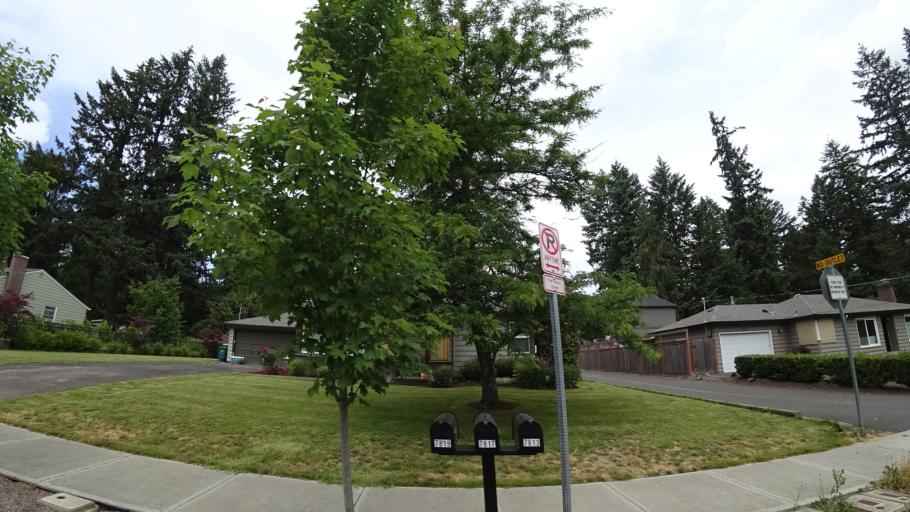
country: US
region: Oregon
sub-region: Washington County
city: Garden Home-Whitford
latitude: 45.4590
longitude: -122.7577
